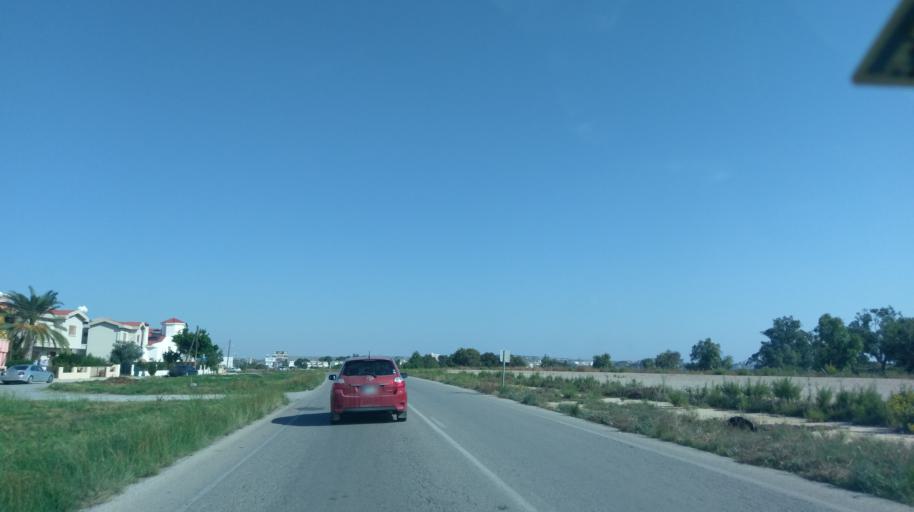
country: CY
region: Ammochostos
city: Trikomo
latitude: 35.3210
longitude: 33.9606
